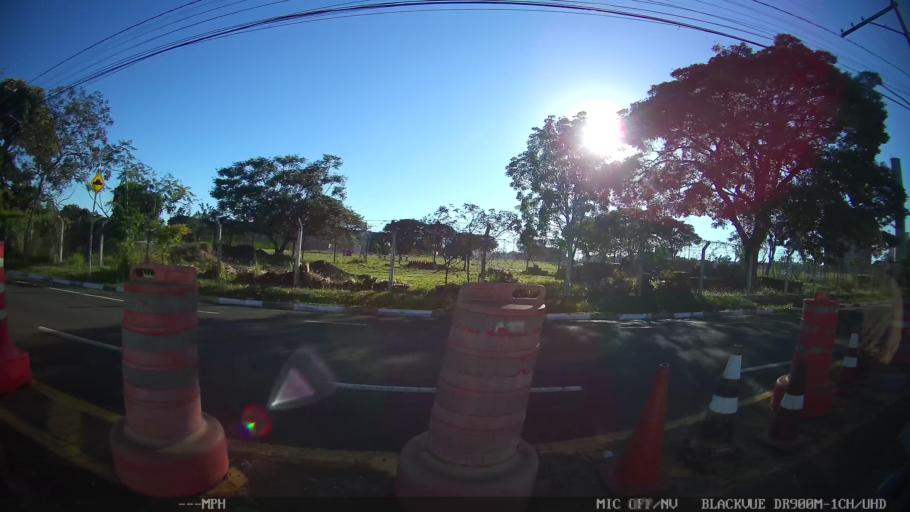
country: BR
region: Sao Paulo
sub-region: Franca
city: Franca
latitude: -20.5631
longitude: -47.4078
